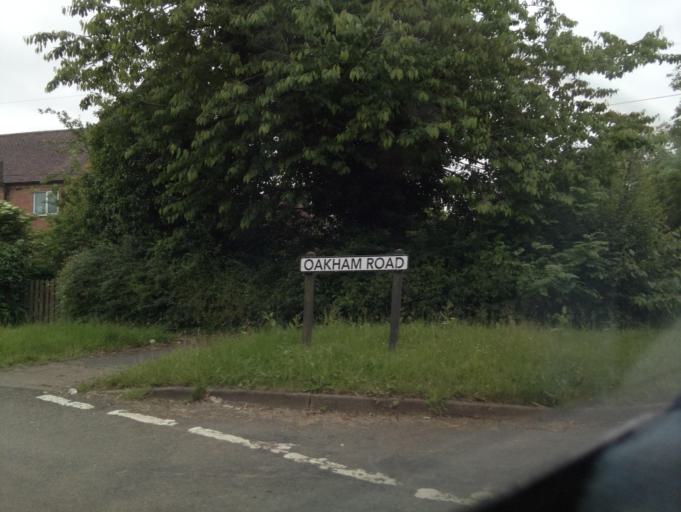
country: GB
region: England
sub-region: District of Rutland
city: Langham
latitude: 52.6854
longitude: -0.8445
